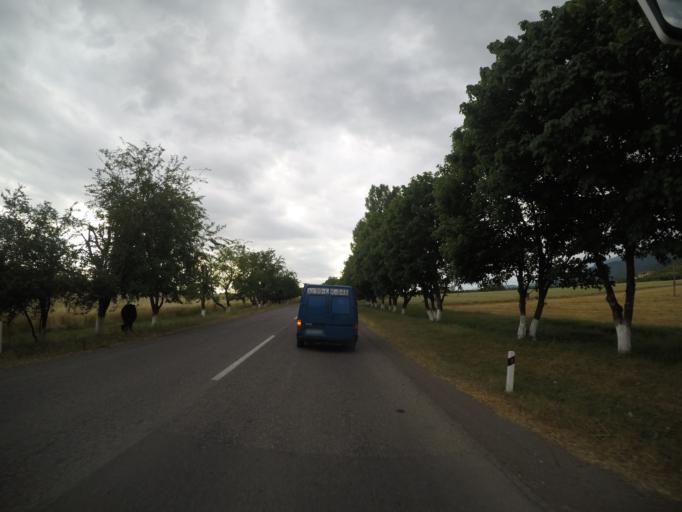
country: AZ
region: Ismayilli
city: Ismayilli
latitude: 40.7728
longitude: 48.2027
